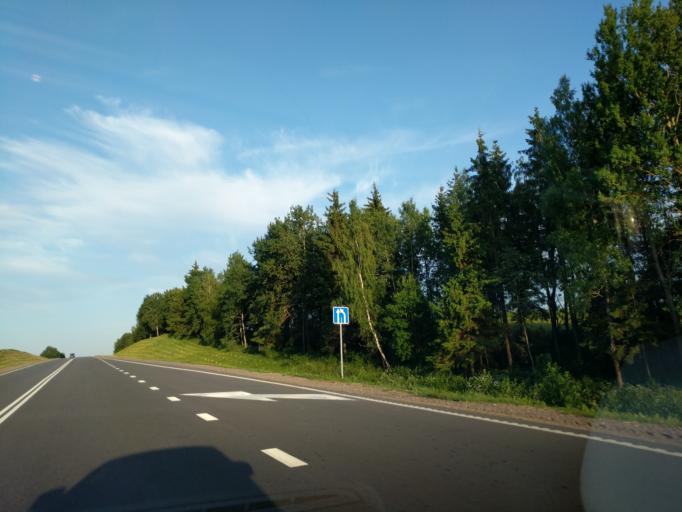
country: BY
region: Minsk
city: Bal'shavik
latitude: 54.0926
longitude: 27.5200
